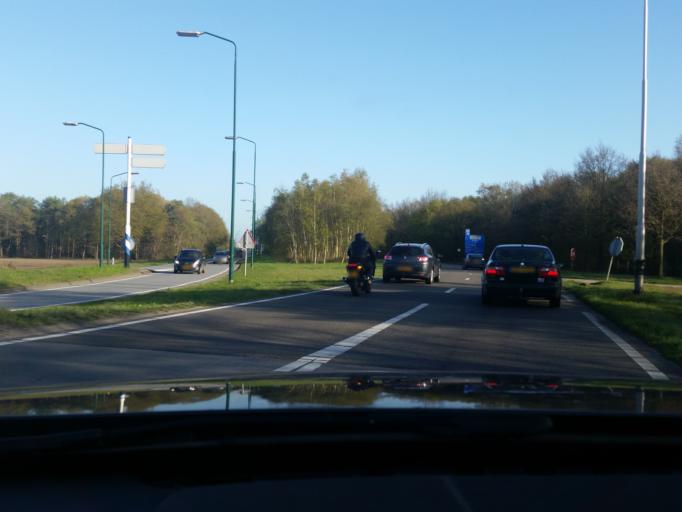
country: NL
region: North Brabant
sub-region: Gemeente Eersel
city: Eersel
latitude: 51.3672
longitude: 5.3260
